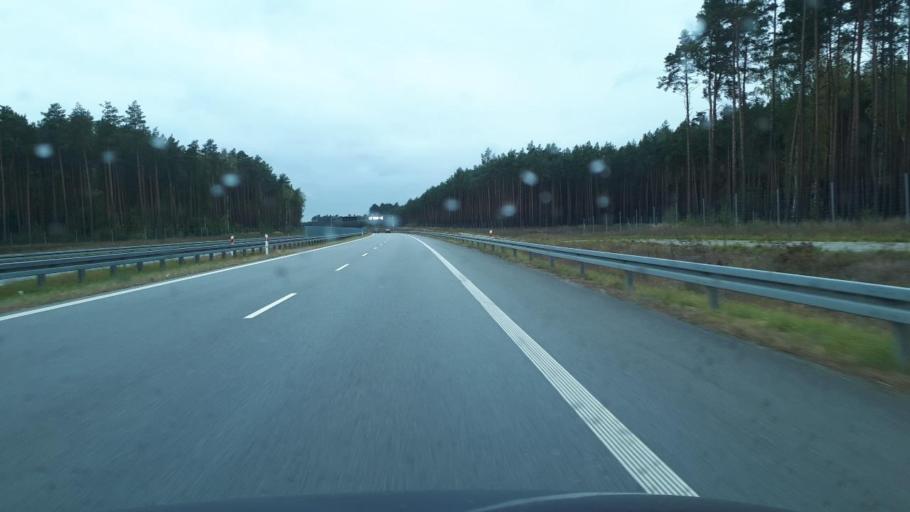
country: PL
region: Greater Poland Voivodeship
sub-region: Powiat kepinski
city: Kepno
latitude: 51.3274
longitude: 17.9862
